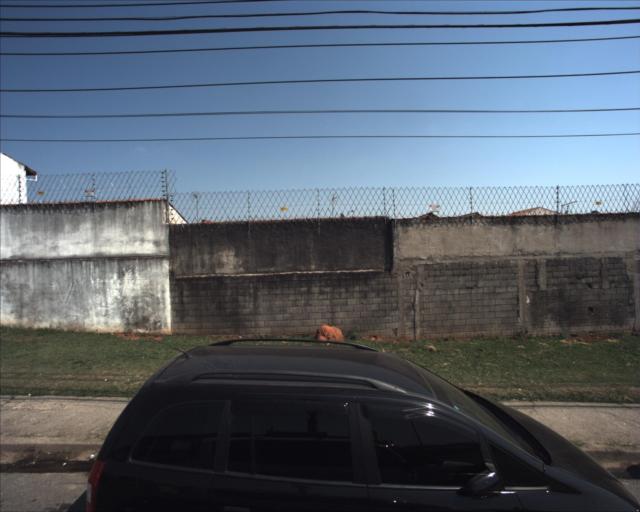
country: BR
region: Sao Paulo
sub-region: Sorocaba
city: Sorocaba
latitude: -23.4520
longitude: -47.4836
